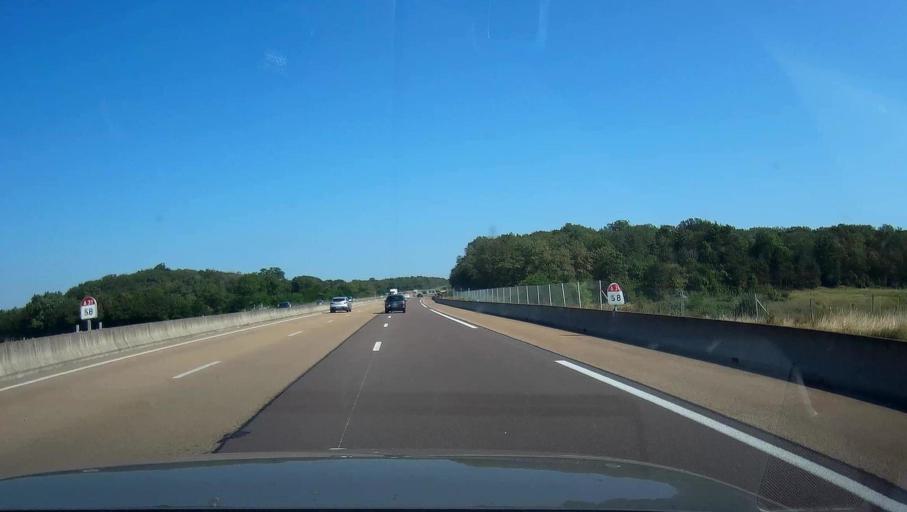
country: FR
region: Bourgogne
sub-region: Departement de la Cote-d'Or
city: Saint-Julien
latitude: 47.4356
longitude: 5.1671
